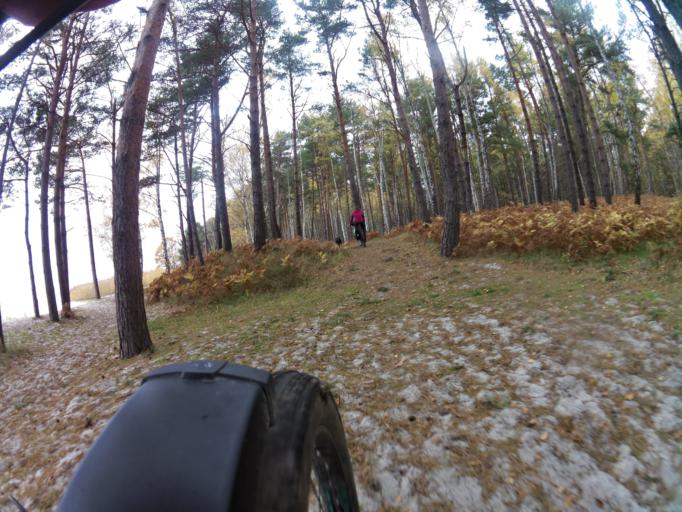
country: PL
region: Pomeranian Voivodeship
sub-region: Powiat pucki
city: Jastarnia
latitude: 54.6863
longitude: 18.7045
